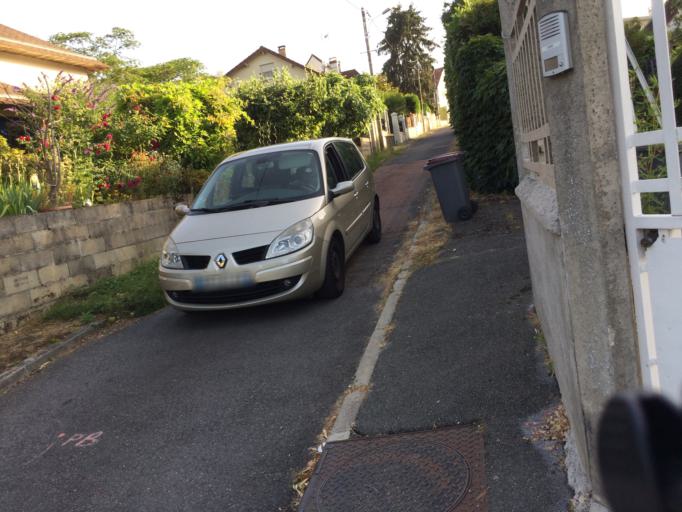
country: FR
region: Ile-de-France
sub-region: Departement de l'Essonne
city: Igny
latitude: 48.7405
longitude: 2.2296
